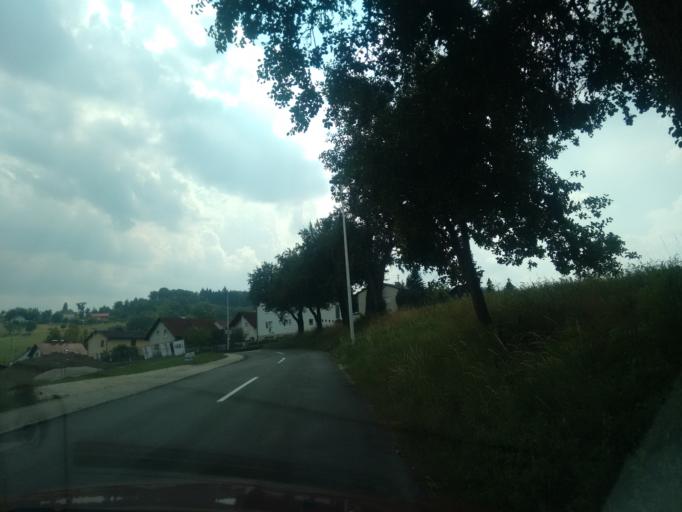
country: AT
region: Upper Austria
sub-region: Politischer Bezirk Grieskirchen
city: Bad Schallerbach
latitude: 48.2415
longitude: 13.9128
